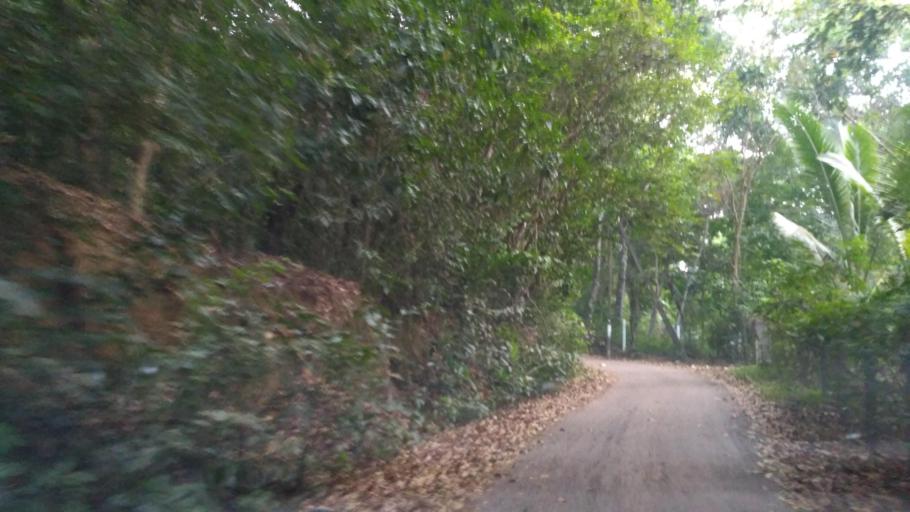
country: LK
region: North Western
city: Kuliyapitiya
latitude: 7.3364
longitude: 80.0042
